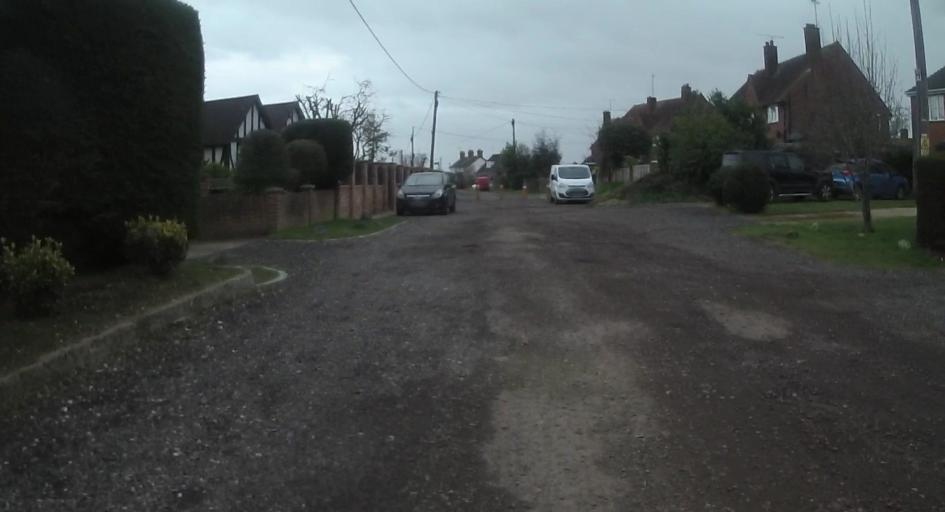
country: GB
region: England
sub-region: Wokingham
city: Shinfield
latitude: 51.4089
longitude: -0.9441
